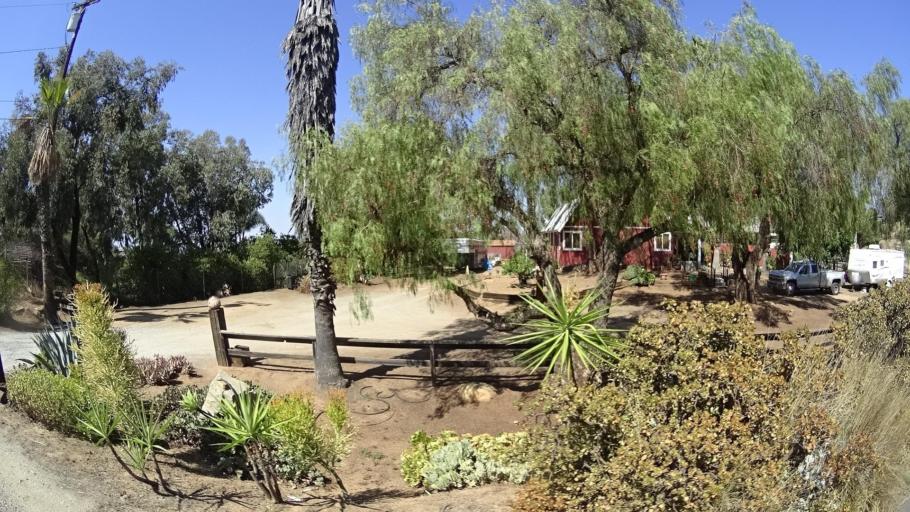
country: US
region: California
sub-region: San Diego County
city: Crest
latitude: 32.8186
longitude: -116.8552
